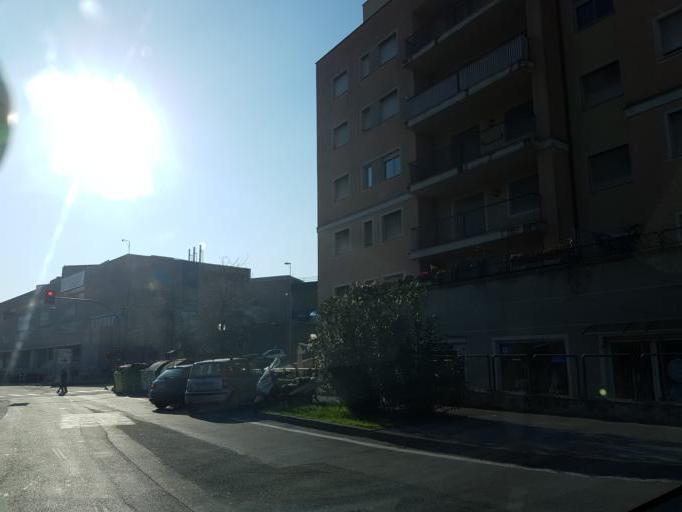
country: IT
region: Liguria
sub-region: Provincia di Genova
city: Manesseno
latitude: 44.4744
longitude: 8.8993
